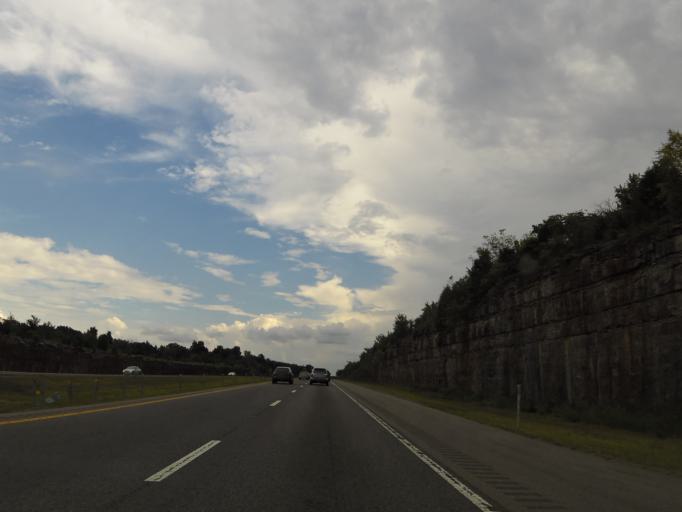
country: US
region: Tennessee
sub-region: Rutherford County
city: Smyrna
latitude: 35.9508
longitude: -86.4411
